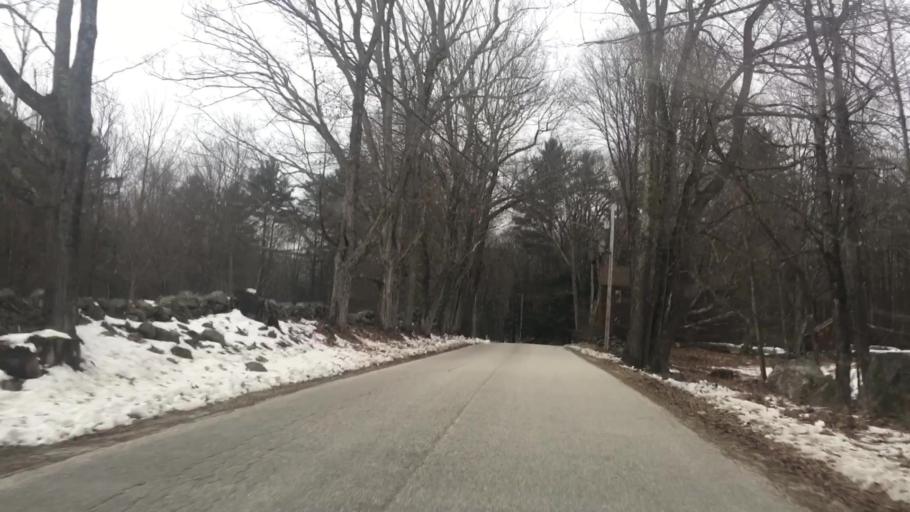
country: US
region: New Hampshire
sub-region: Merrimack County
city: Hopkinton
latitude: 43.1672
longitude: -71.6700
